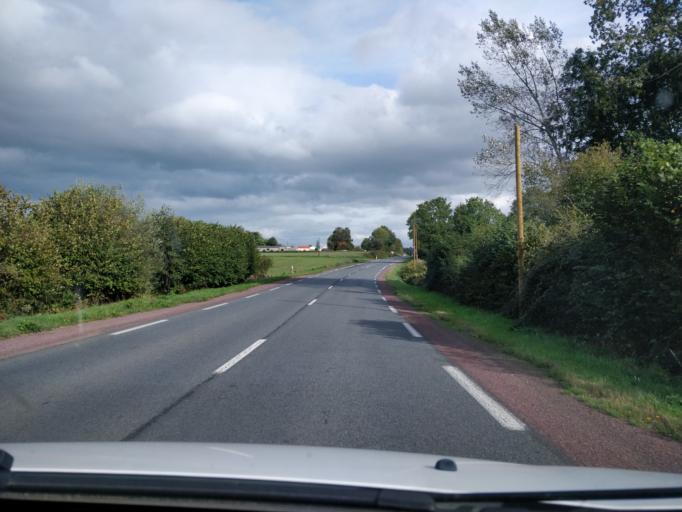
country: FR
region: Lower Normandy
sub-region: Departement du Calvados
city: Saint-Sever-Calvados
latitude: 48.8403
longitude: -0.9933
